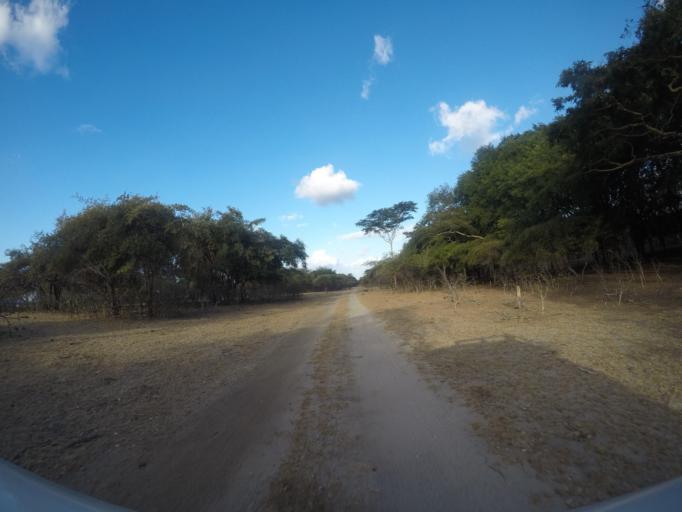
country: TL
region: Lautem
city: Lospalos
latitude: -8.3260
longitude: 126.9807
